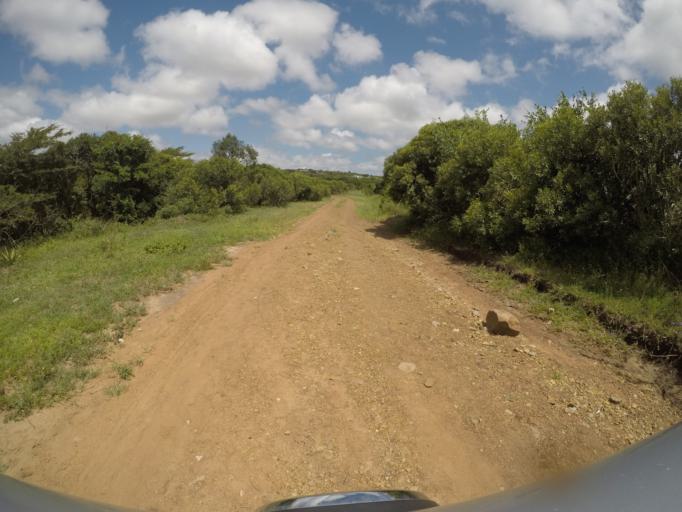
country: ZA
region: KwaZulu-Natal
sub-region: uThungulu District Municipality
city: Empangeni
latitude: -28.5798
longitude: 31.8371
